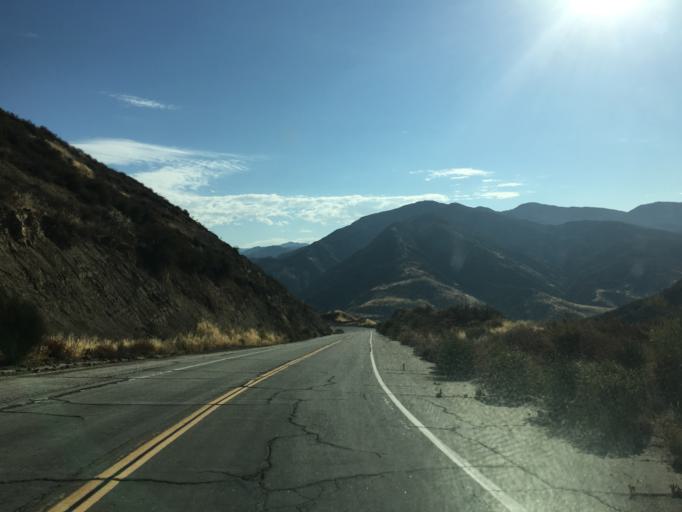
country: US
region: California
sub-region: Los Angeles County
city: Castaic
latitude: 34.5944
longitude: -118.6746
